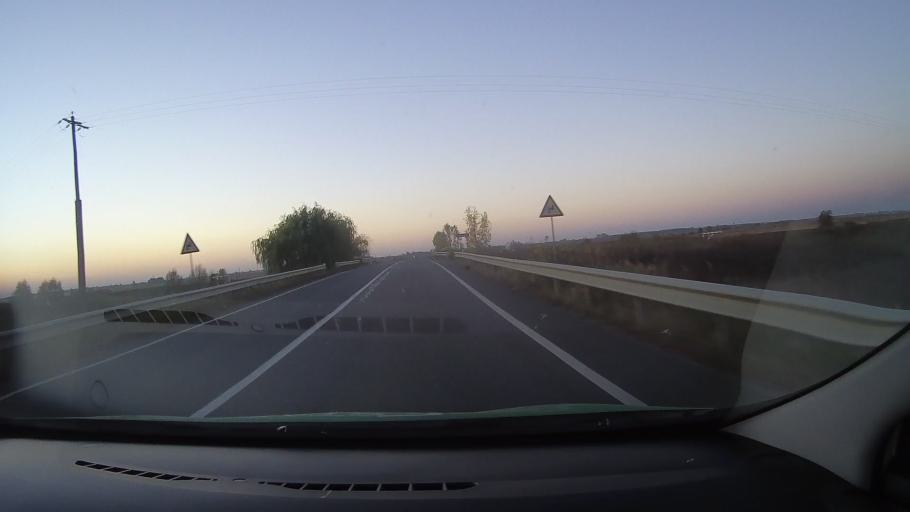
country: RO
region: Bihor
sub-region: Comuna Tarcea
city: Tarcea
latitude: 47.4454
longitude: 22.1879
